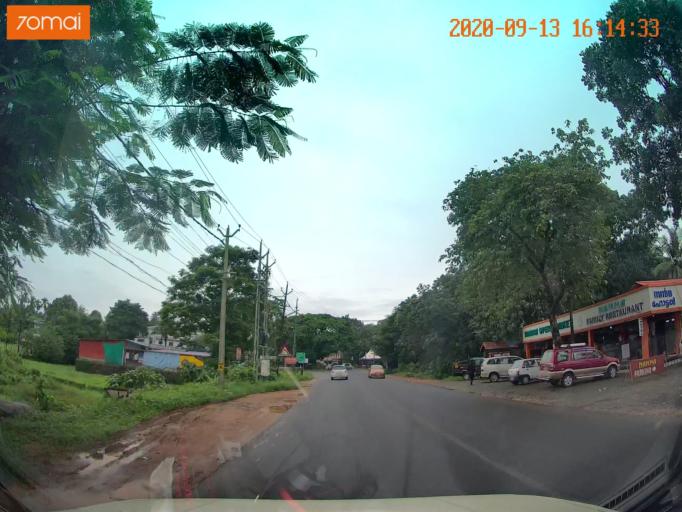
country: IN
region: Kerala
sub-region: Kottayam
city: Palackattumala
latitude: 9.6895
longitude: 76.6360
